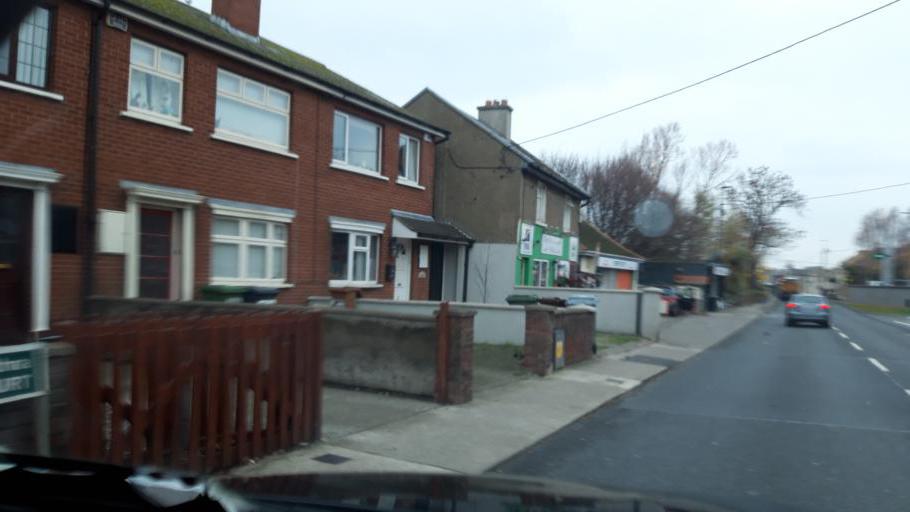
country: IE
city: Milltown
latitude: 53.3024
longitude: -6.2452
